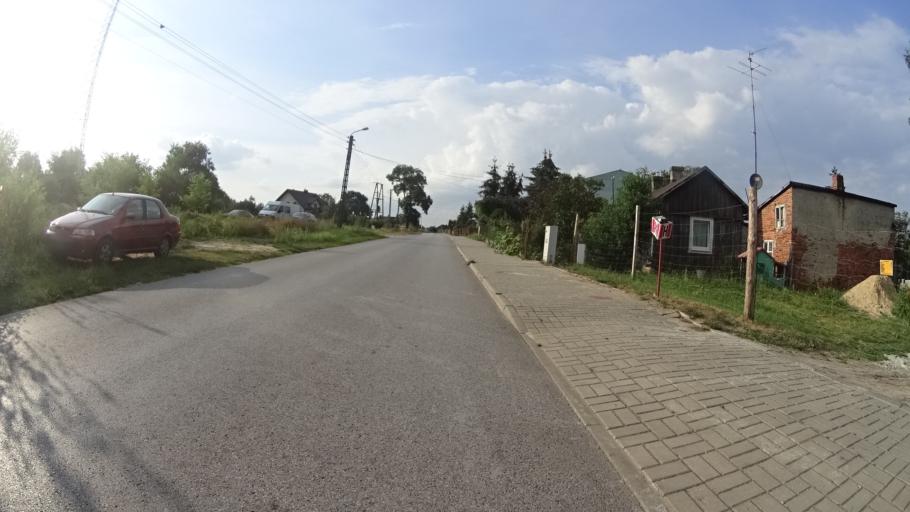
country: PL
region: Masovian Voivodeship
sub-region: Powiat grojecki
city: Mogielnica
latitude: 51.6850
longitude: 20.7309
